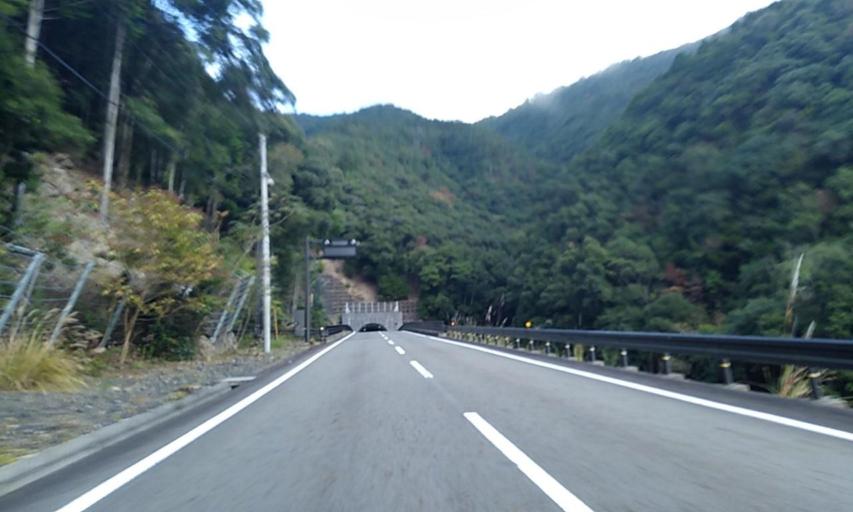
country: JP
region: Wakayama
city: Shingu
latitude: 33.8793
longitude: 135.8766
